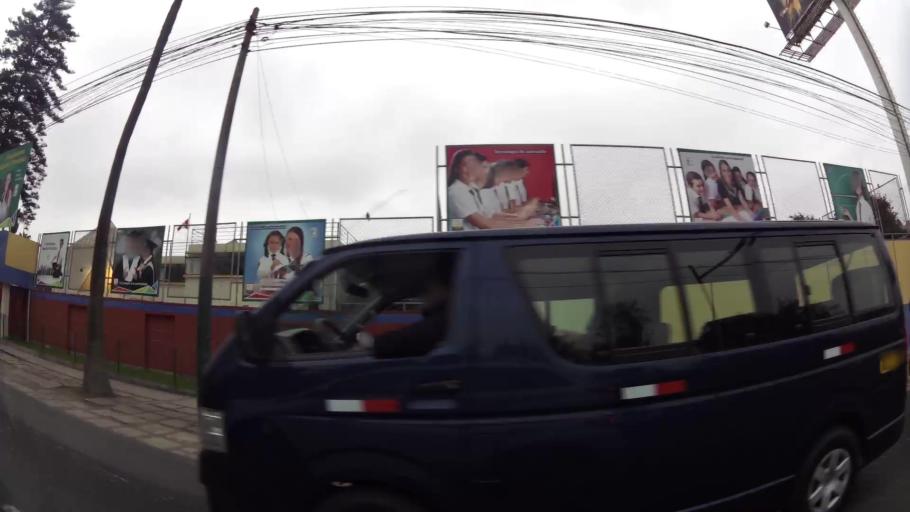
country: PE
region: Lima
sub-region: Lima
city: La Molina
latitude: -12.0982
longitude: -76.9739
